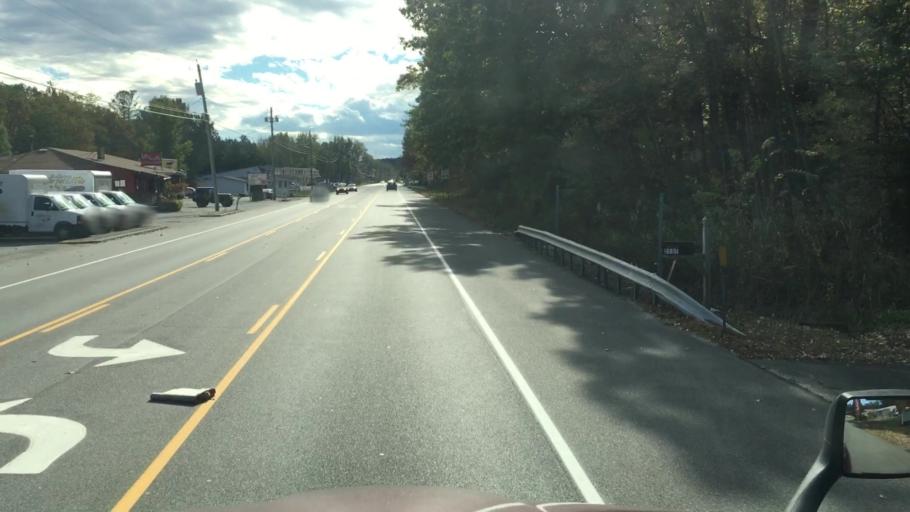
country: US
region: New York
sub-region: Saratoga County
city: North Ballston Spa
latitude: 43.0186
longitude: -73.8429
